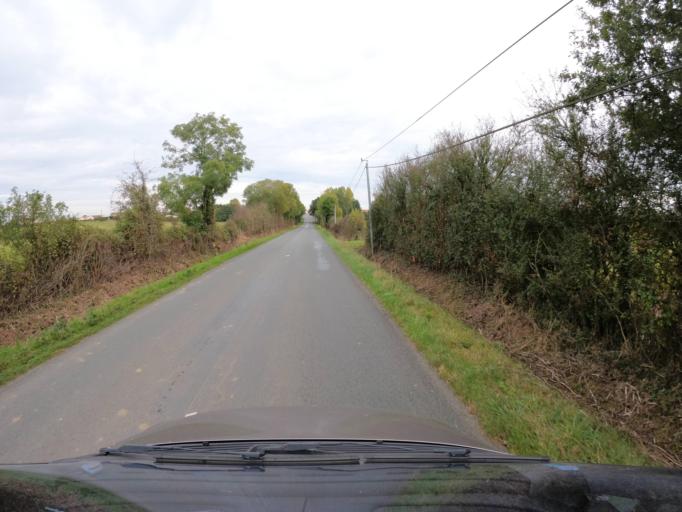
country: FR
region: Pays de la Loire
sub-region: Departement de Maine-et-Loire
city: Saint-Christophe-du-Bois
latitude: 47.0262
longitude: -0.9529
